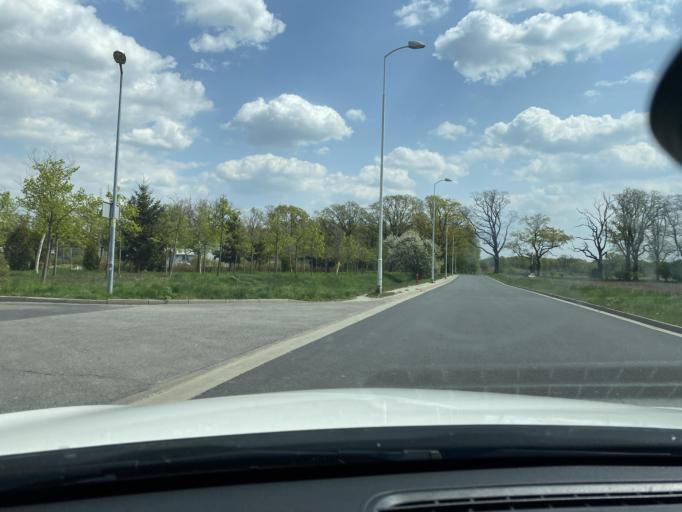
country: PL
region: Lower Silesian Voivodeship
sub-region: Powiat trzebnicki
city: Psary
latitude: 51.1522
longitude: 16.9966
